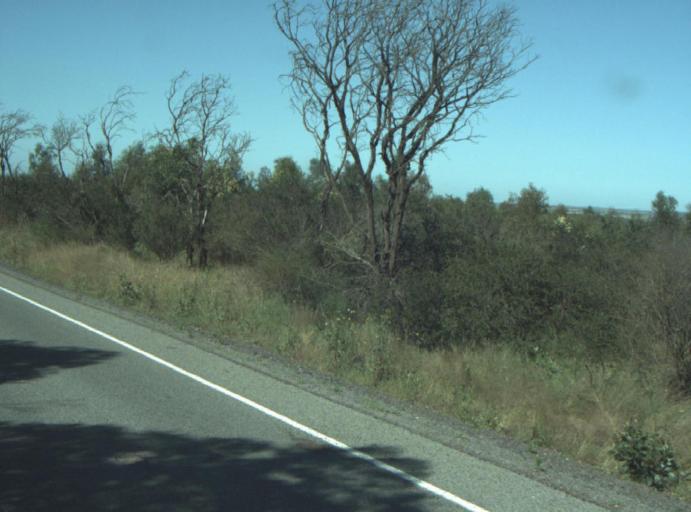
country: AU
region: Victoria
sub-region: Greater Geelong
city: Lara
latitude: -37.9088
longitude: 144.3988
